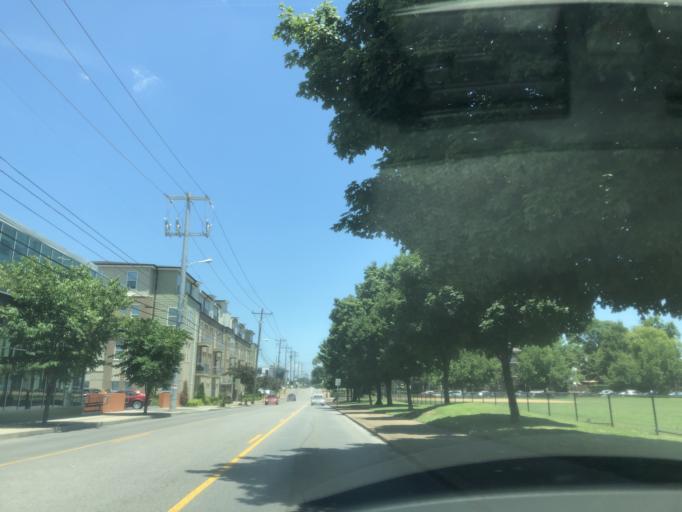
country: US
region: Tennessee
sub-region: Davidson County
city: Nashville
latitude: 36.1736
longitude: -86.7601
